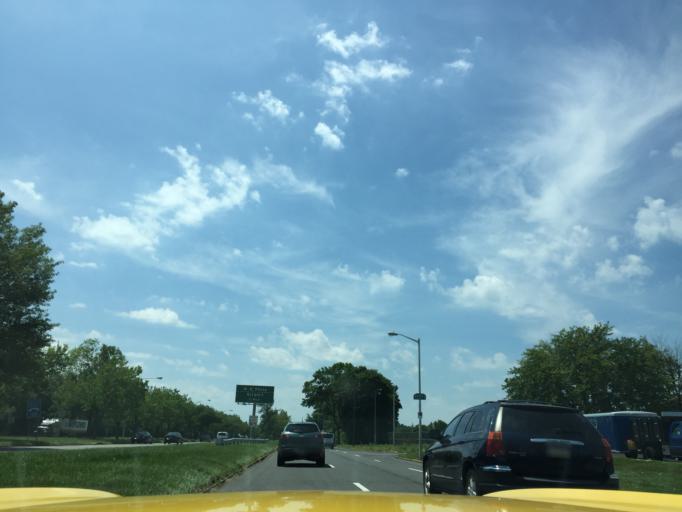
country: US
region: Pennsylvania
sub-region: Bucks County
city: Feasterville
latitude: 40.0934
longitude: -75.0169
